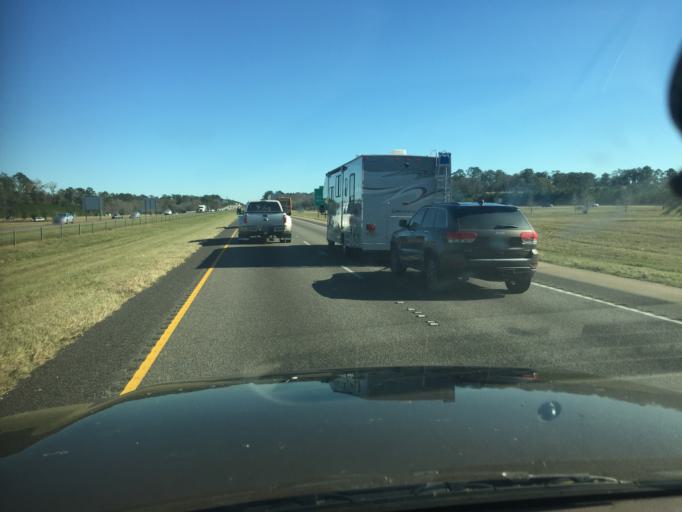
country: US
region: Louisiana
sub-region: Saint Tammany Parish
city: Covington
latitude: 30.4421
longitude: -90.1260
